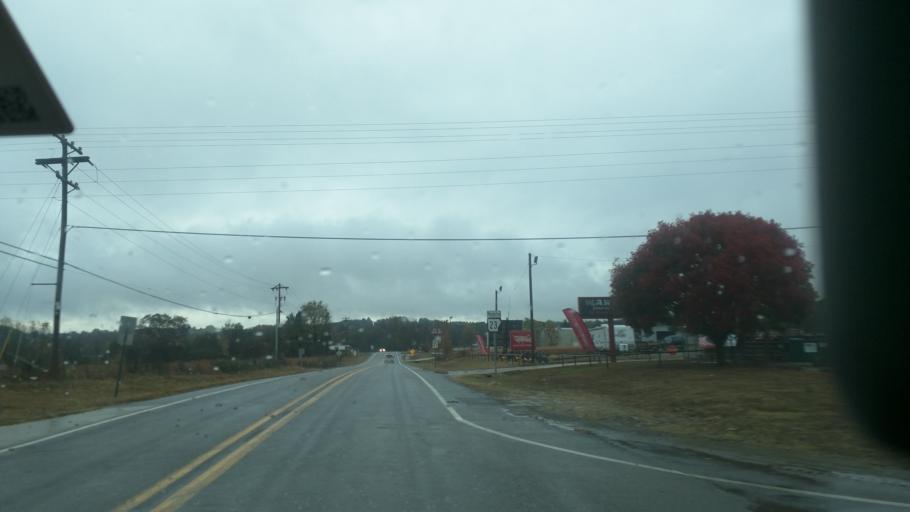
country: US
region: Arkansas
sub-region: Franklin County
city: Ozark
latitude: 35.5043
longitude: -93.8455
